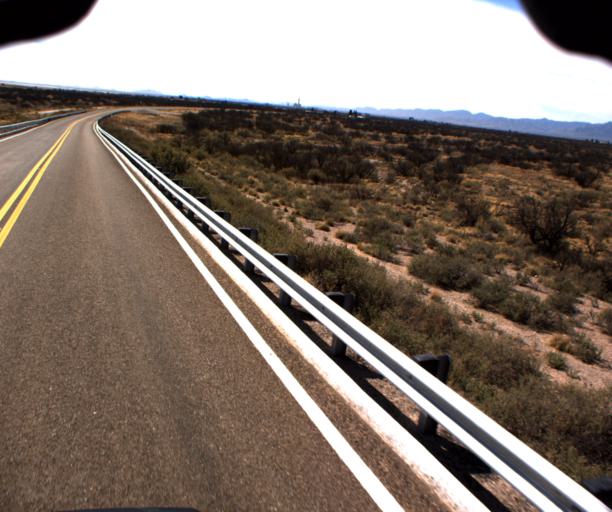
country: US
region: Arizona
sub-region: Cochise County
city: Willcox
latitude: 32.1328
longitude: -109.9102
